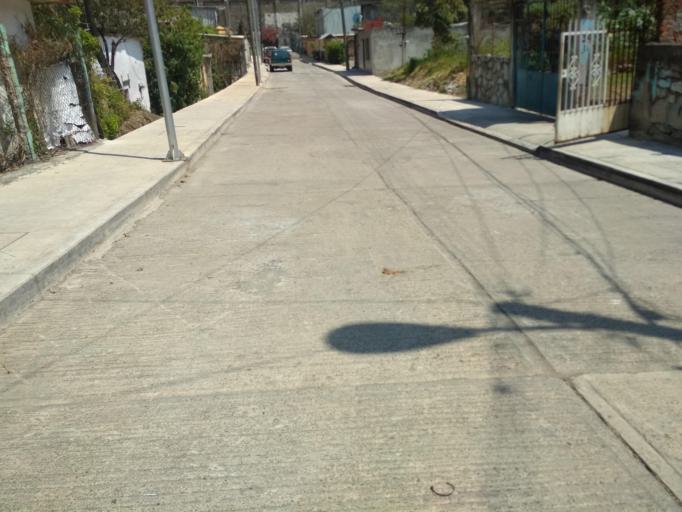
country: MX
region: Veracruz
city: Rio Blanco
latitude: 18.8390
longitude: -97.1121
